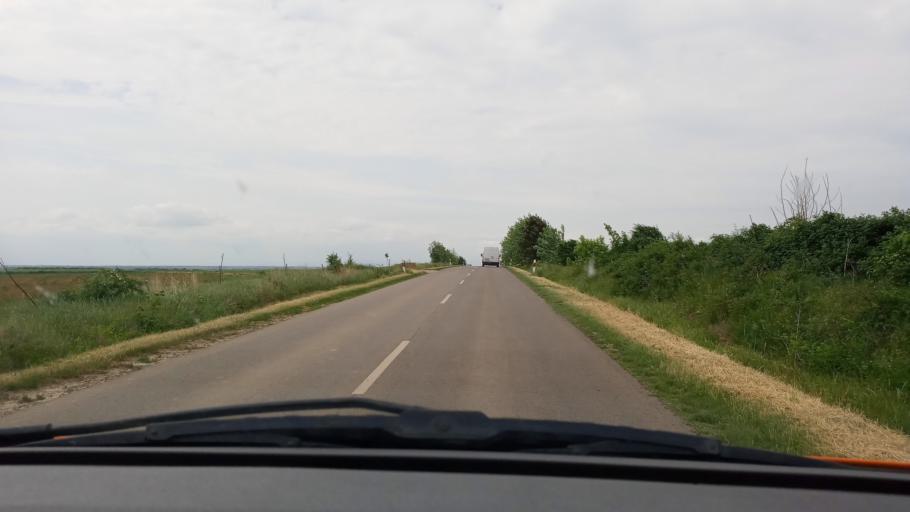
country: HU
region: Baranya
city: Vajszlo
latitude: 45.9384
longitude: 18.0726
